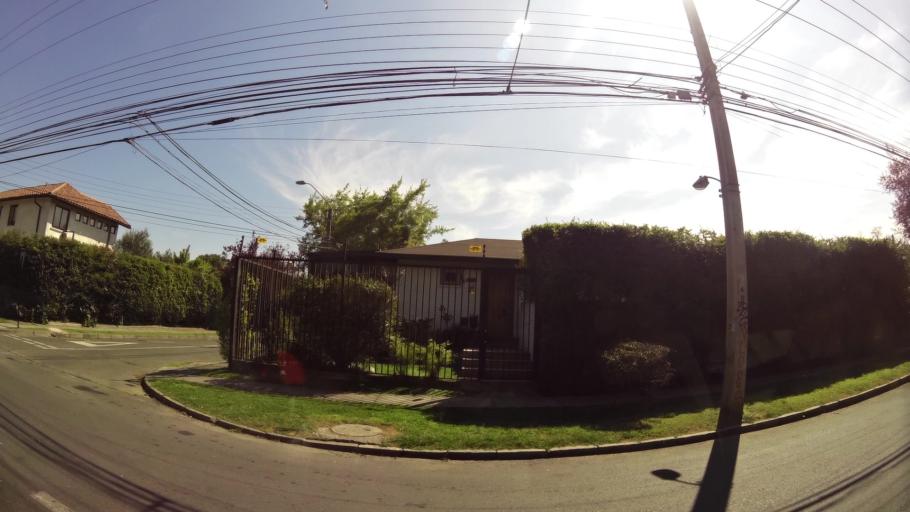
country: CL
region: Santiago Metropolitan
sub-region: Provincia de Santiago
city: Villa Presidente Frei, Nunoa, Santiago, Chile
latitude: -33.4462
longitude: -70.5471
